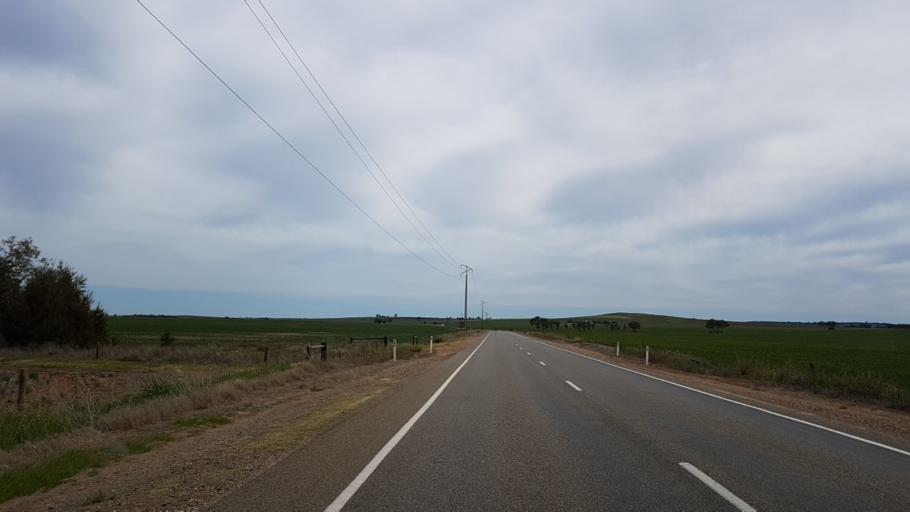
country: AU
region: South Australia
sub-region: Port Pirie City and Dists
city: Crystal Brook
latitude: -33.2652
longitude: 138.3307
